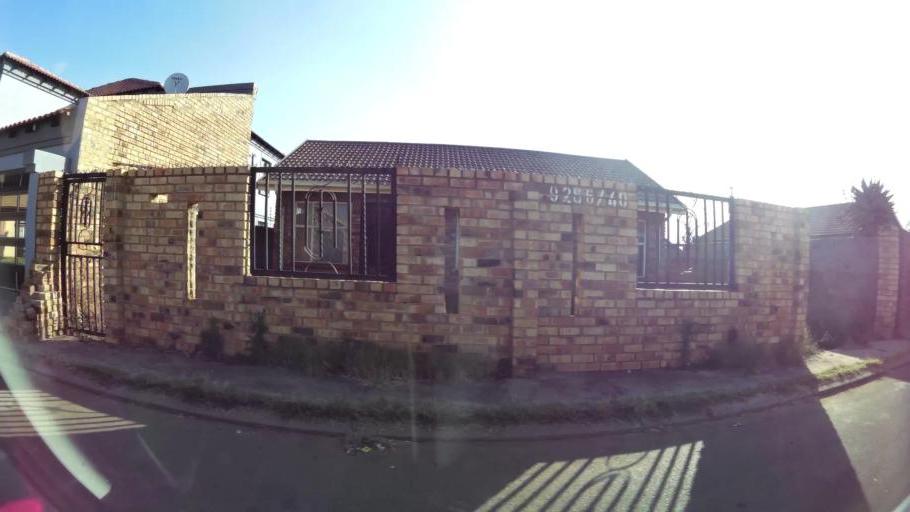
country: ZA
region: Gauteng
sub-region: City of Johannesburg Metropolitan Municipality
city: Soweto
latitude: -26.2680
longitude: 27.9155
